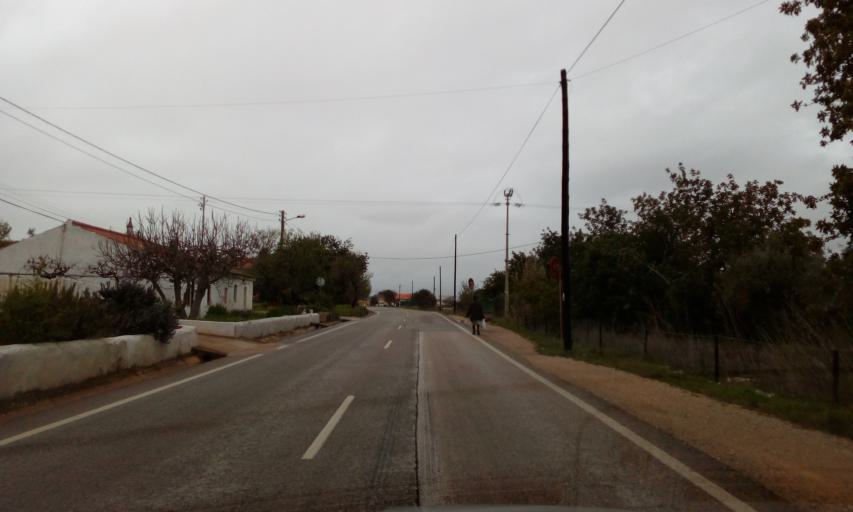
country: PT
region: Faro
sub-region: Albufeira
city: Guia
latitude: 37.1540
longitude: -8.2784
